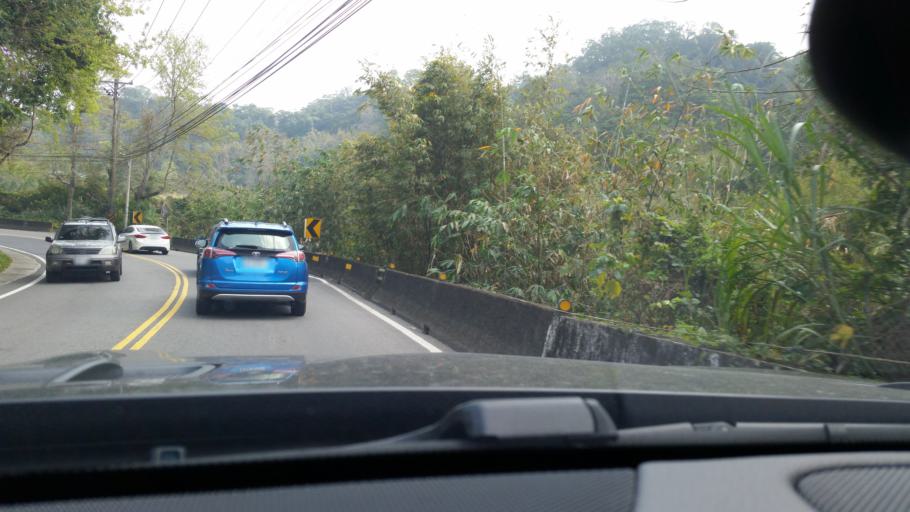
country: TW
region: Taiwan
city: Daxi
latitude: 24.8279
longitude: 121.3137
